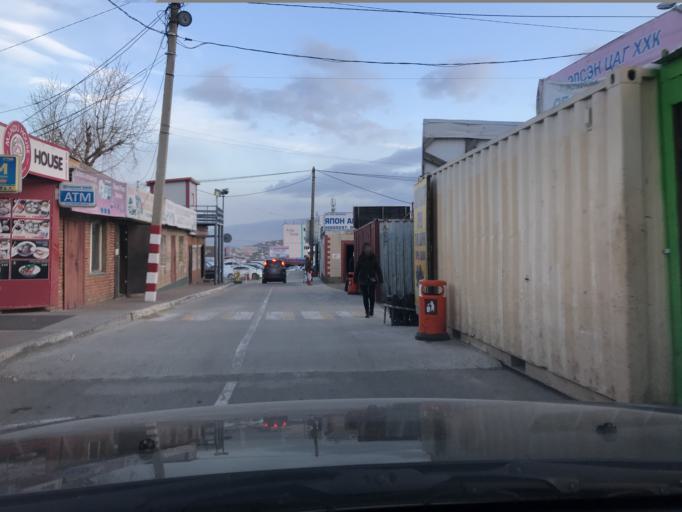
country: MN
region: Ulaanbaatar
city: Ulaanbaatar
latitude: 47.9305
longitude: 107.0012
